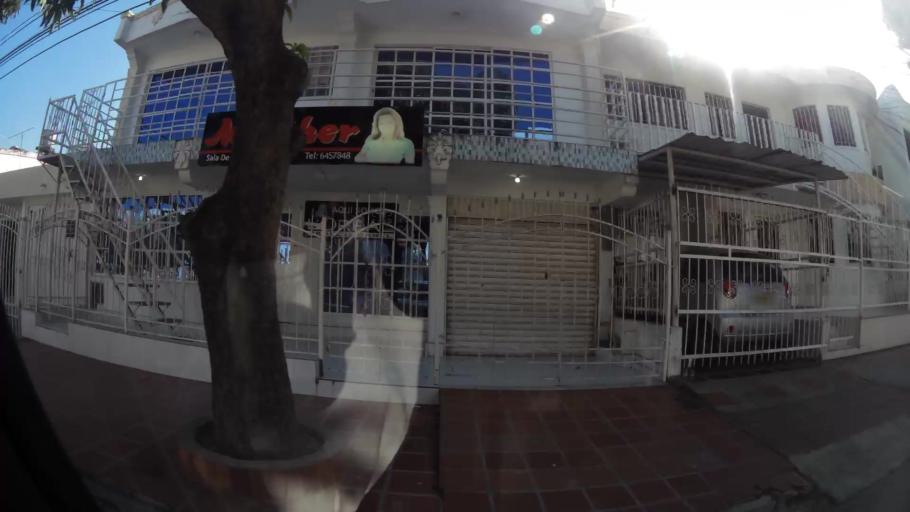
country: CO
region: Bolivar
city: Cartagena
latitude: 10.3918
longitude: -75.4941
